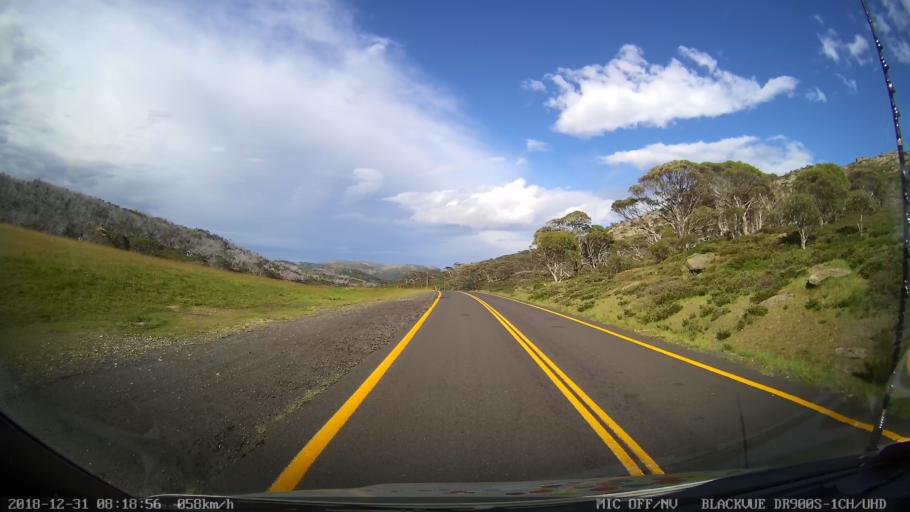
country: AU
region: New South Wales
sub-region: Snowy River
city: Jindabyne
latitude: -36.4164
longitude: 148.3916
